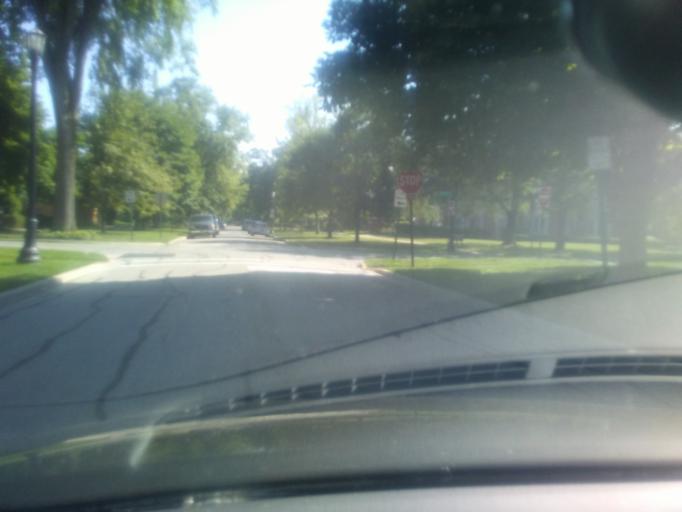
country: US
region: Illinois
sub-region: Cook County
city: Wilmette
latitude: 42.0611
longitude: -87.7057
